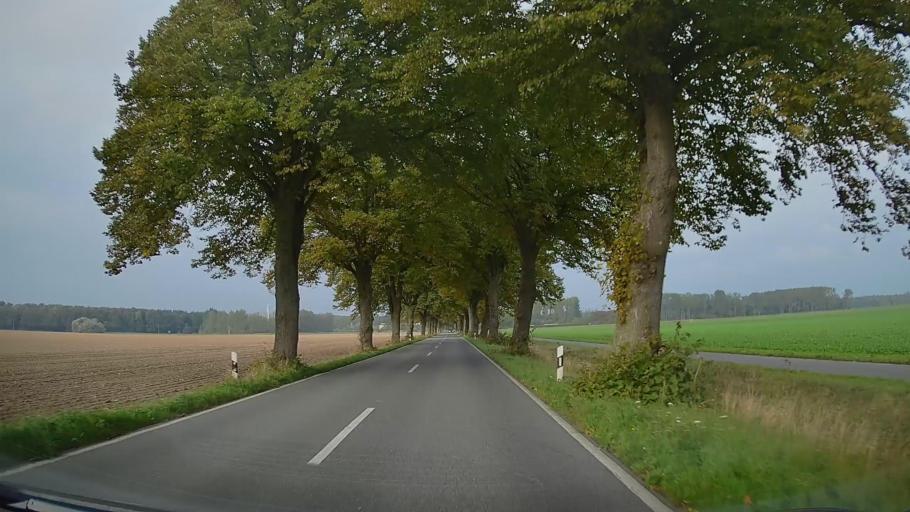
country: DE
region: Mecklenburg-Vorpommern
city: Bad Doberan
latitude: 54.1323
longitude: 11.8344
